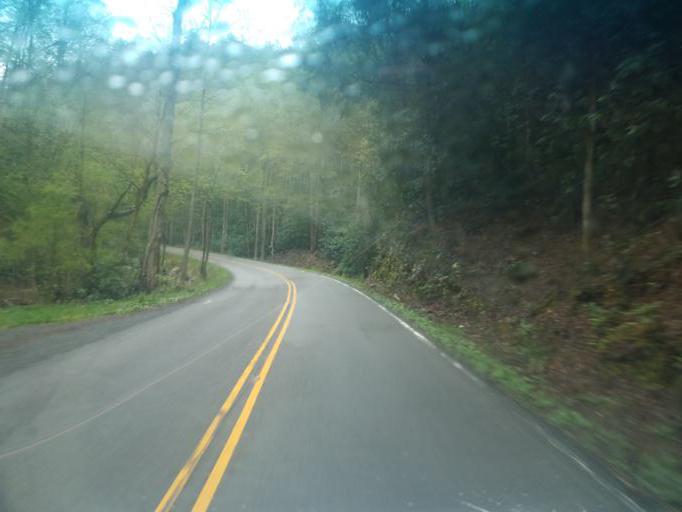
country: US
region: Virginia
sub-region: Washington County
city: Glade Spring
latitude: 36.6451
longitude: -81.7217
